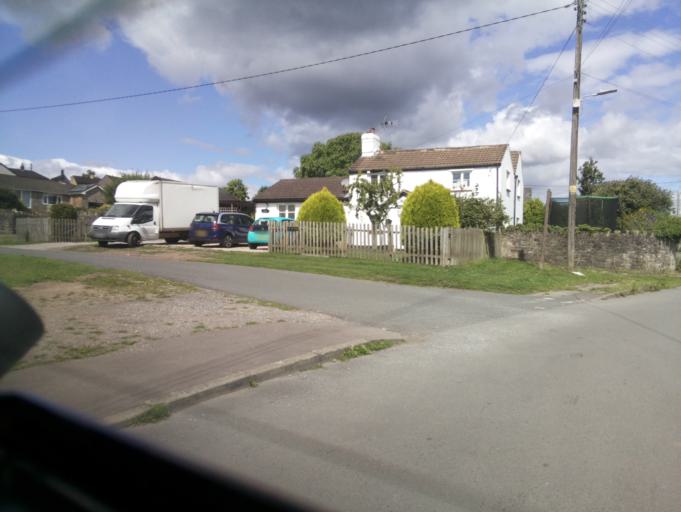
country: GB
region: England
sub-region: Gloucestershire
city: Bream
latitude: 51.7494
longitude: -2.5692
